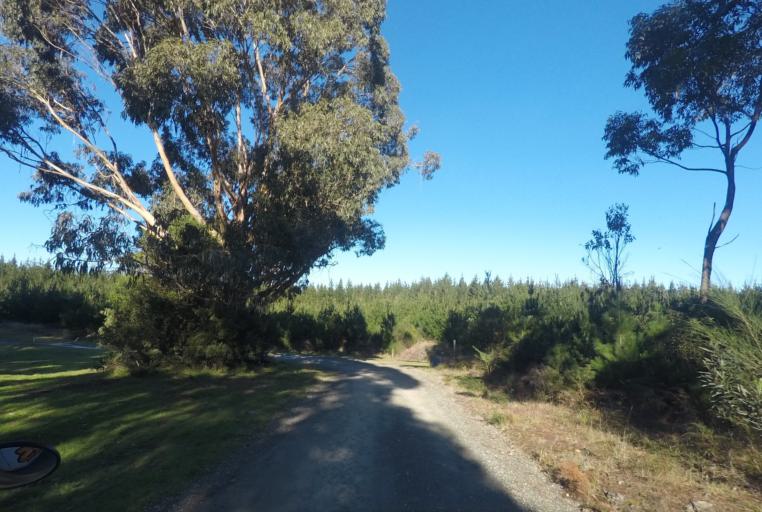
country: NZ
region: Tasman
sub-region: Tasman District
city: Mapua
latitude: -41.2643
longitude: 173.1427
